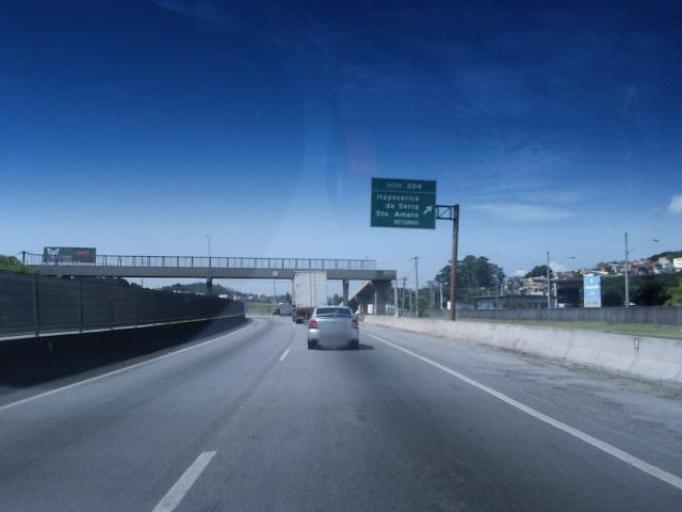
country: BR
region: Sao Paulo
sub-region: Embu
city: Embu
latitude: -23.6786
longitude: -46.8583
